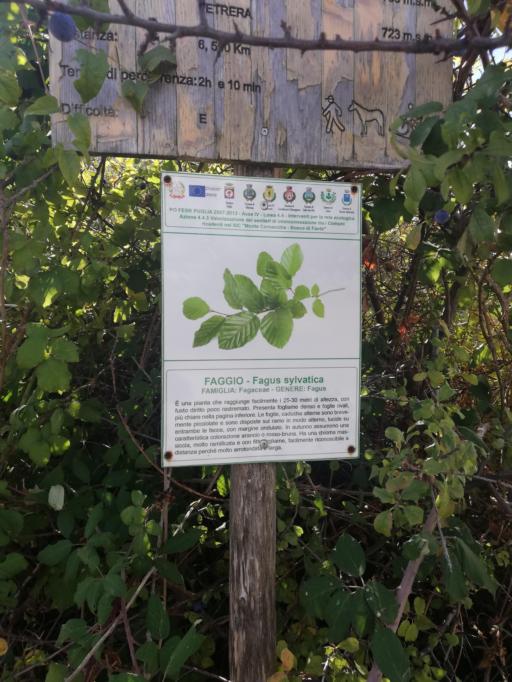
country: IT
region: Apulia
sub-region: Provincia di Foggia
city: Biccari
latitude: 41.3800
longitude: 15.1823
